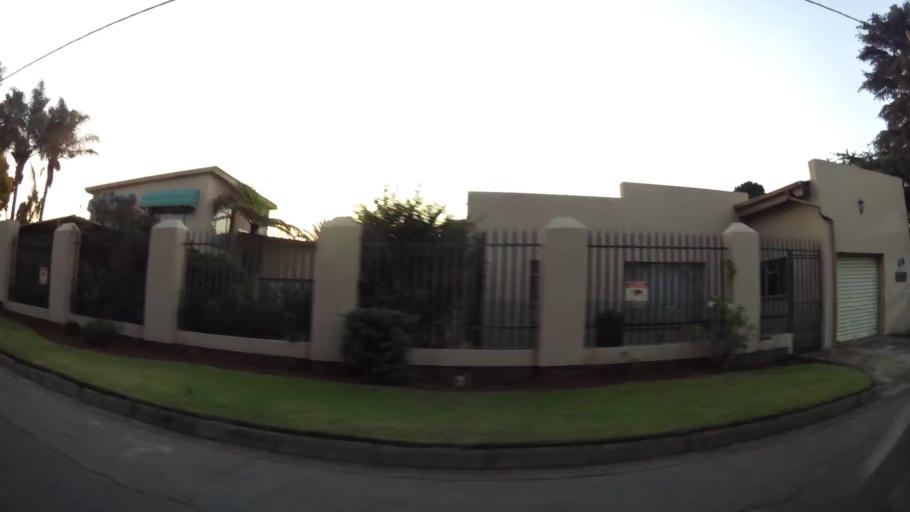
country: ZA
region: Gauteng
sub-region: Ekurhuleni Metropolitan Municipality
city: Tembisa
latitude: -26.0595
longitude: 28.2317
